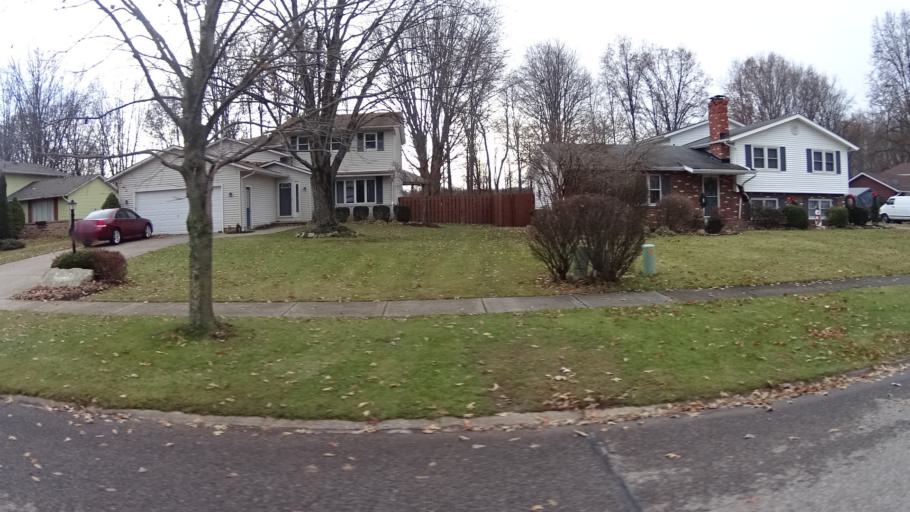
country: US
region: Ohio
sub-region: Lorain County
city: North Ridgeville
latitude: 41.3702
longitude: -82.0239
